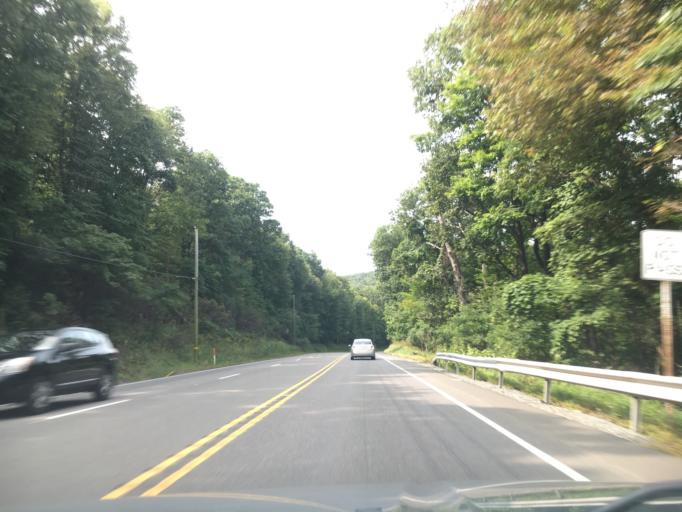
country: US
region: Pennsylvania
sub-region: Carbon County
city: Summit Hill
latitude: 40.7079
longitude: -75.8213
